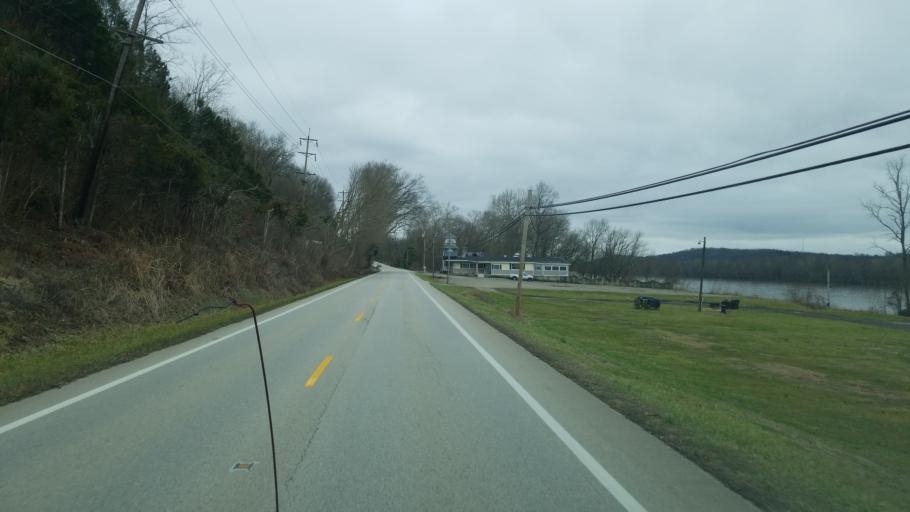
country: US
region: Ohio
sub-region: Clermont County
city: New Richmond
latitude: 38.9132
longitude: -84.2483
